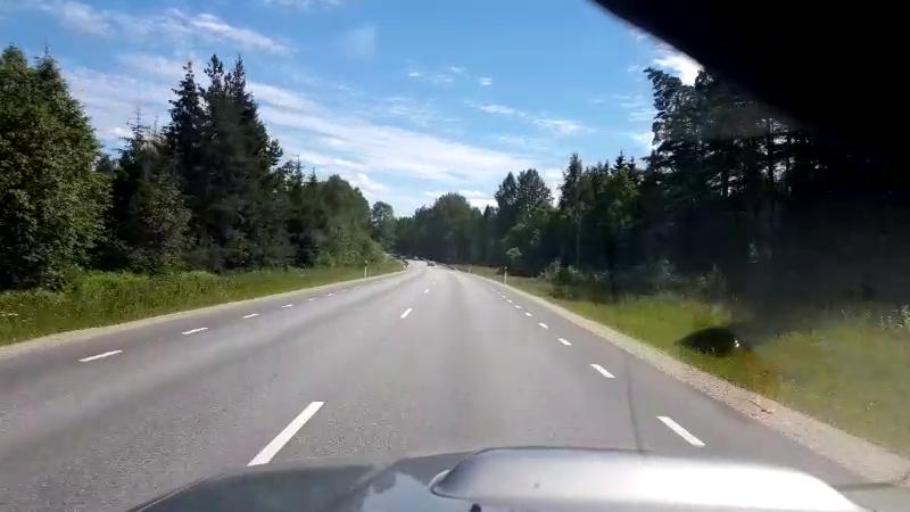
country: EE
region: Jogevamaa
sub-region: Jogeva linn
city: Jogeva
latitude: 58.7891
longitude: 26.3116
